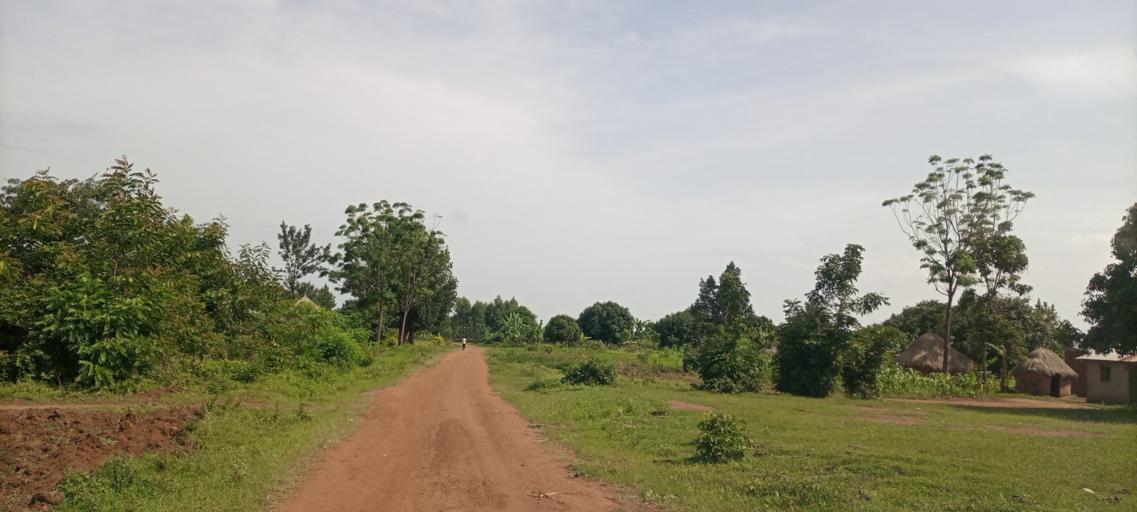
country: UG
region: Eastern Region
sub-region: Budaka District
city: Budaka
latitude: 1.1322
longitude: 34.0215
